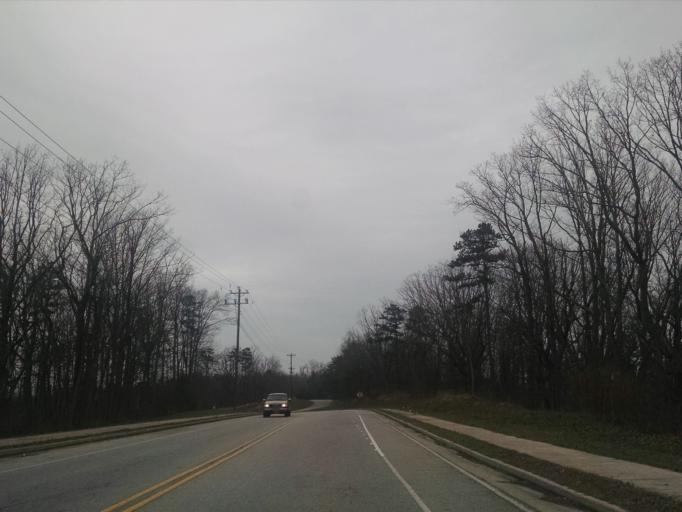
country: US
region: Georgia
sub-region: Hall County
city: Flowery Branch
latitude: 34.1892
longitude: -83.8967
